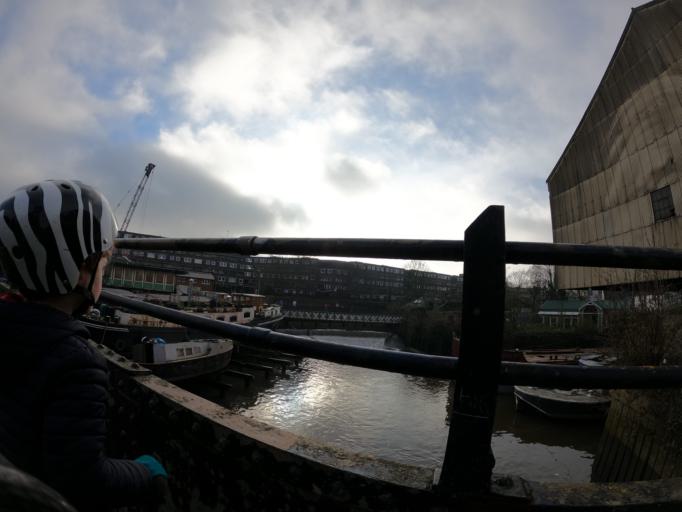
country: GB
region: England
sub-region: Greater London
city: Brentford
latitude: 51.4827
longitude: -0.3049
